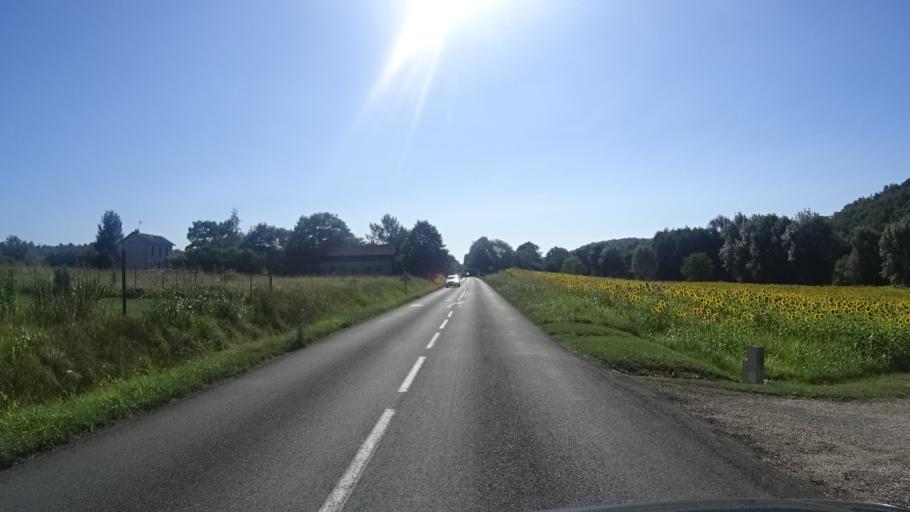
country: FR
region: Aquitaine
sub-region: Departement de la Dordogne
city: Sourzac
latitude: 45.0157
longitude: 0.4445
